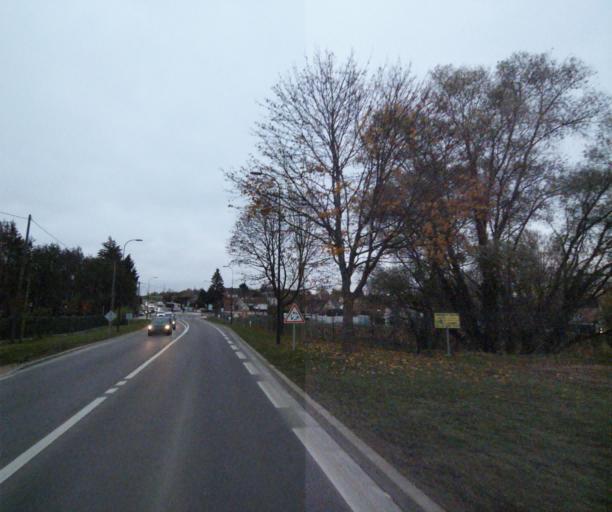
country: FR
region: Ile-de-France
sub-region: Departement des Yvelines
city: Villennes-sur-Seine
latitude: 48.9396
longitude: 1.9774
